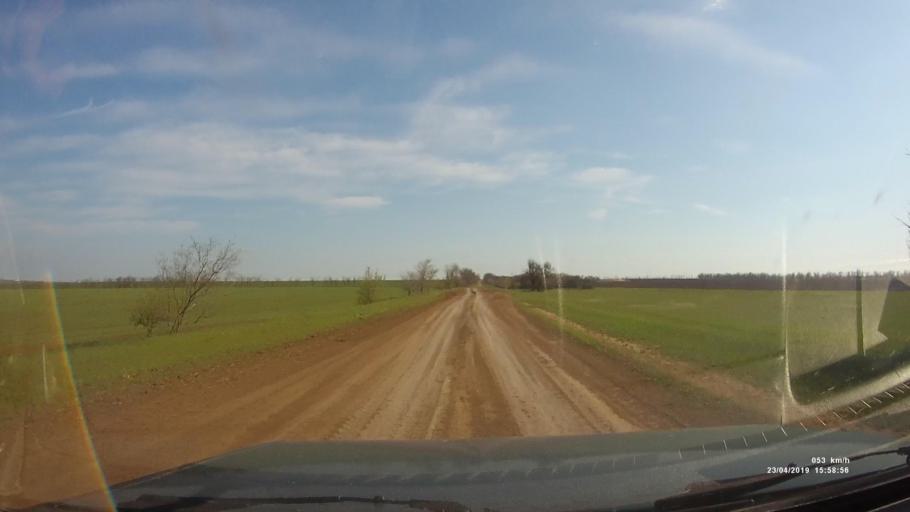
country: RU
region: Rostov
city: Remontnoye
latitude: 46.5202
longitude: 43.1095
